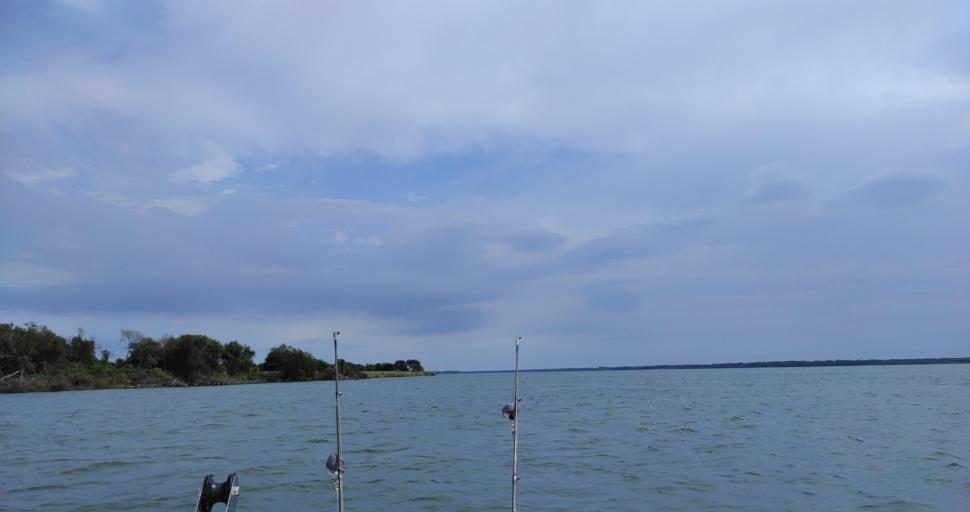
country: PY
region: Neembucu
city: Cerrito
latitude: -27.3555
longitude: -57.6750
